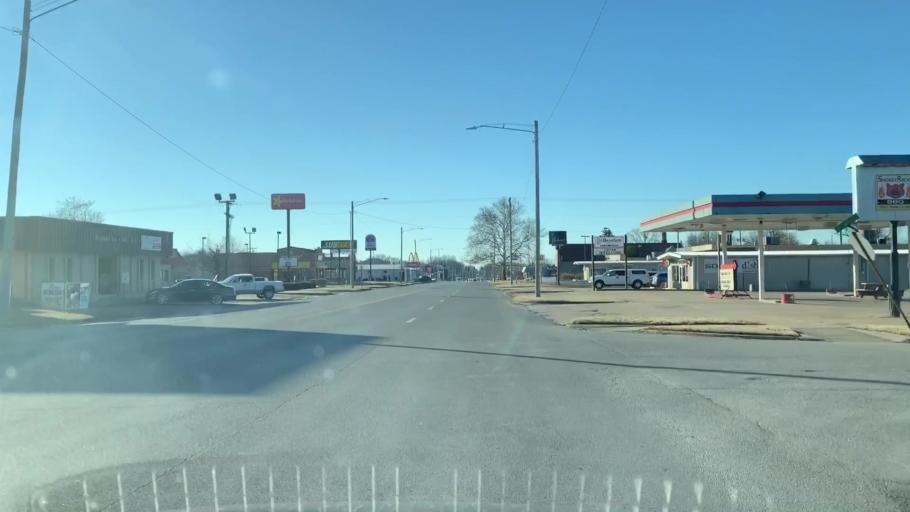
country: US
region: Kansas
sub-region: Crawford County
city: Pittsburg
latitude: 37.3994
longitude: -94.7050
